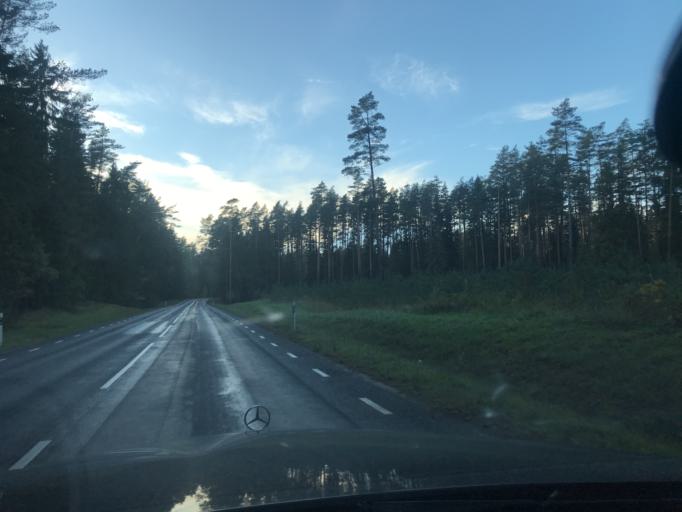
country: EE
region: Vorumaa
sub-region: Antsla vald
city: Vana-Antsla
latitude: 57.8802
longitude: 26.7587
